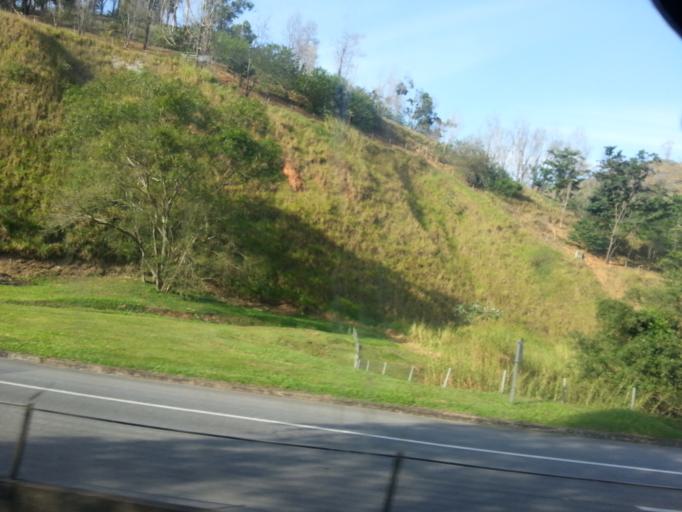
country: BR
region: Rio de Janeiro
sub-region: Pirai
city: Pirai
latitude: -22.6655
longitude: -43.8640
